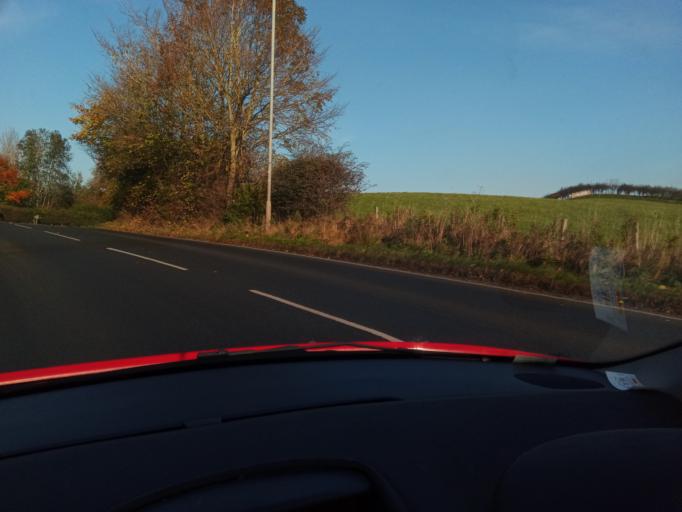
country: GB
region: Scotland
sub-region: The Scottish Borders
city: Hawick
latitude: 55.4372
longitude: -2.7479
